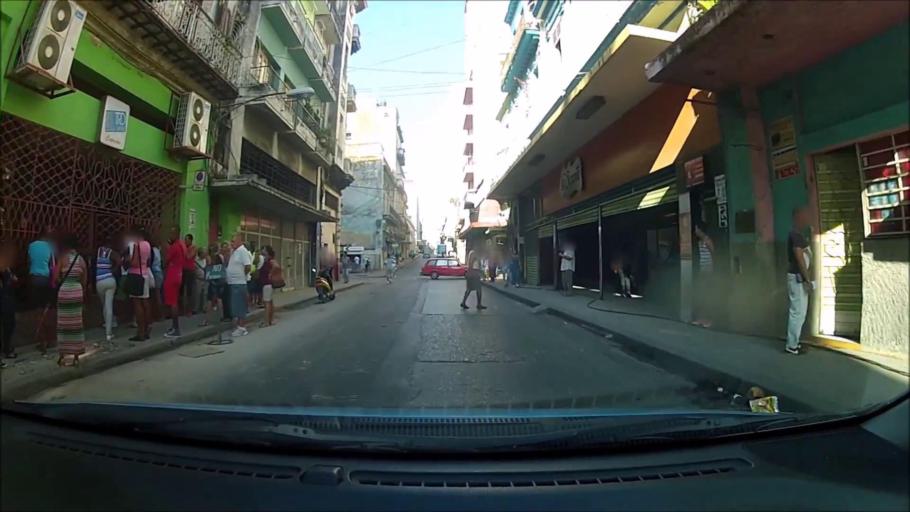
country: CU
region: La Habana
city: Centro Habana
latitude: 23.1377
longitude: -82.3623
